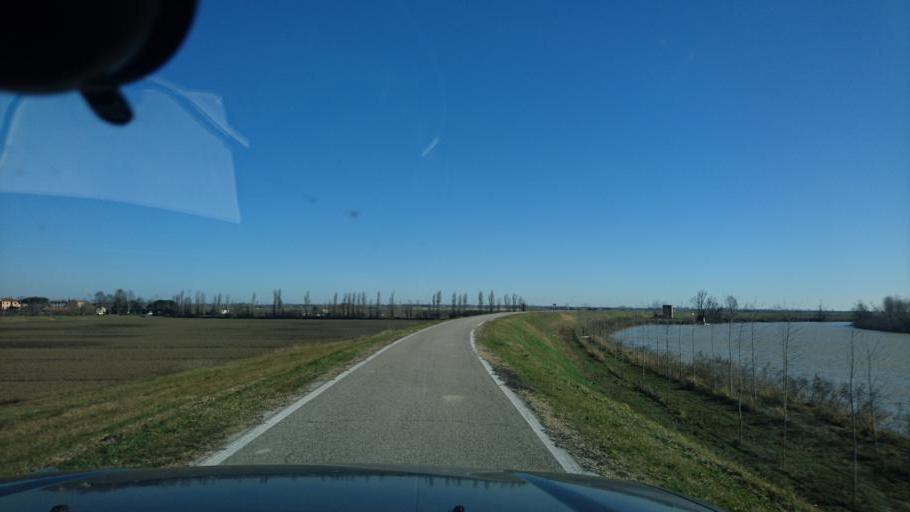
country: IT
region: Veneto
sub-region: Provincia di Rovigo
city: Papozze
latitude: 44.9429
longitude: 12.1701
